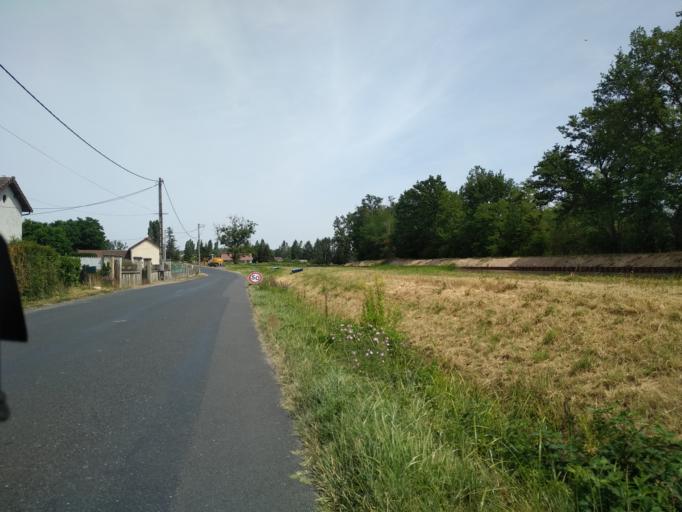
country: FR
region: Bourgogne
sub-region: Departement de Saone-et-Loire
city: Digoin
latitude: 46.4702
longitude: 3.9662
